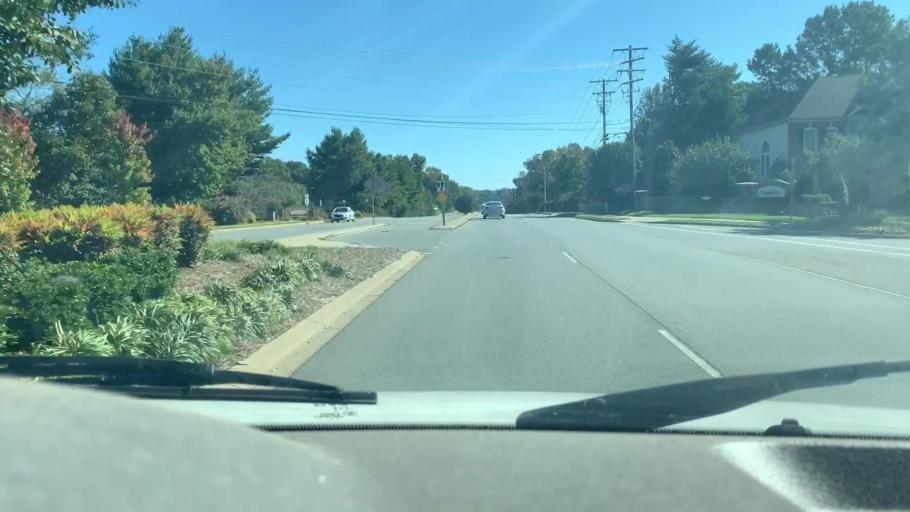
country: US
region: North Carolina
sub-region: Mecklenburg County
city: Huntersville
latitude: 35.4414
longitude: -80.8536
